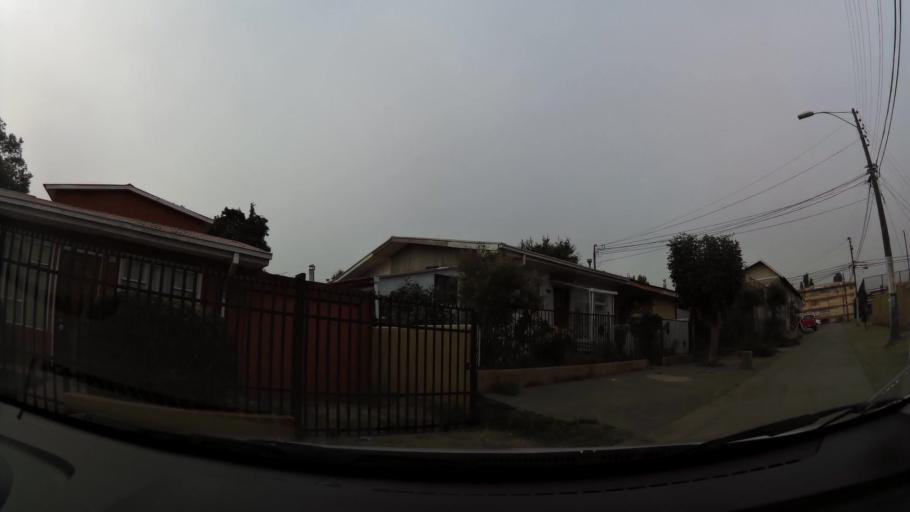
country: CL
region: Biobio
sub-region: Provincia de Concepcion
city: Concepcion
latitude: -36.8021
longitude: -73.0798
